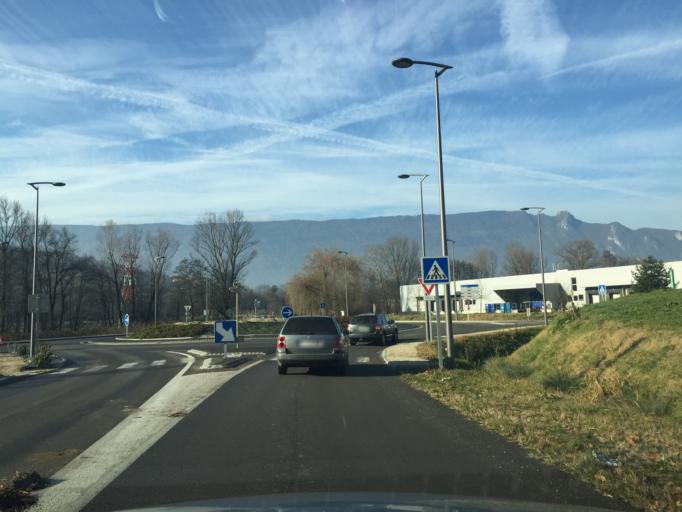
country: FR
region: Rhone-Alpes
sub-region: Departement de la Savoie
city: Voglans
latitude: 45.6428
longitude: 5.9158
